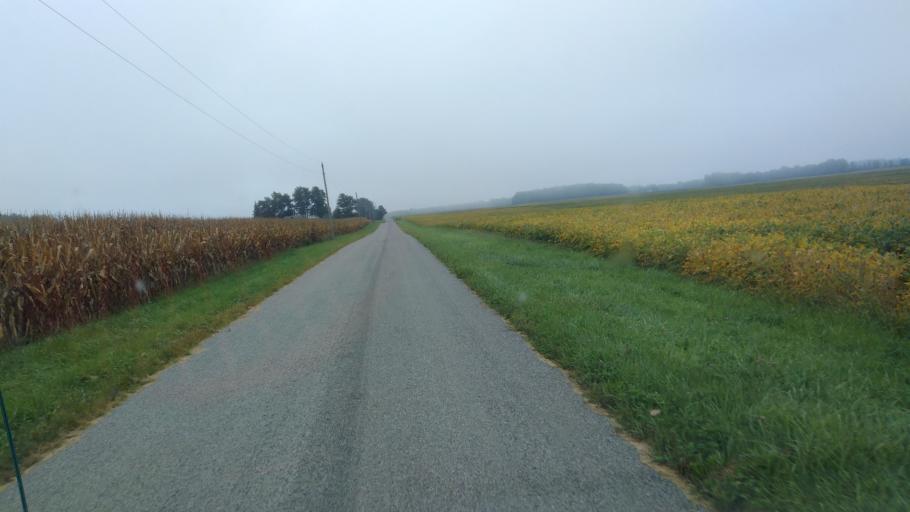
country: US
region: Ohio
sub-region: Union County
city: Richwood
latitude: 40.4983
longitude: -83.4147
